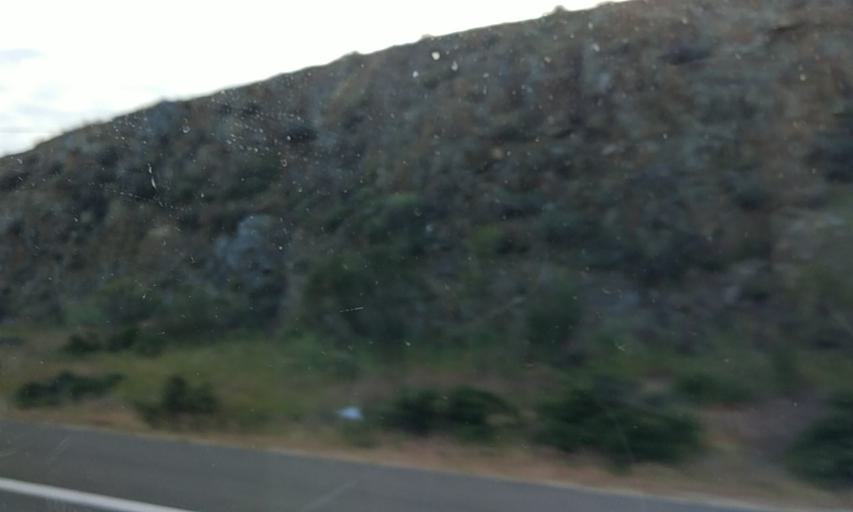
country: ES
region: Extremadura
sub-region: Provincia de Caceres
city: Santiago del Campo
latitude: 39.6098
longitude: -6.4065
